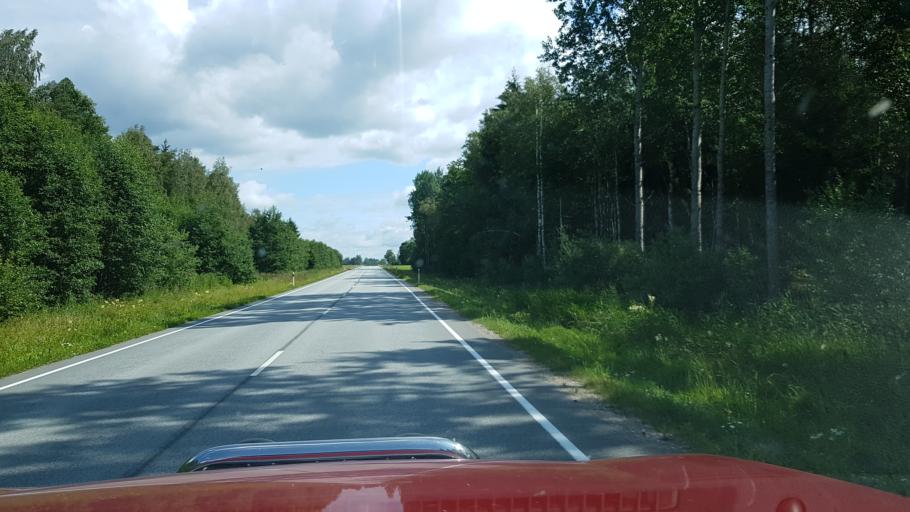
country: EE
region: Jogevamaa
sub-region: Jogeva linn
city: Jogeva
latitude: 58.8181
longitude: 26.5700
